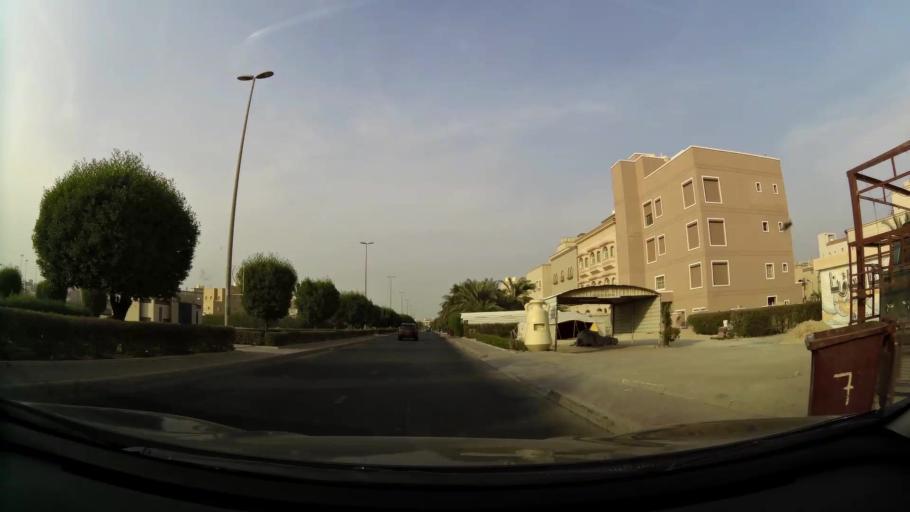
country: KW
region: Mubarak al Kabir
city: Mubarak al Kabir
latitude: 29.1904
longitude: 48.0808
